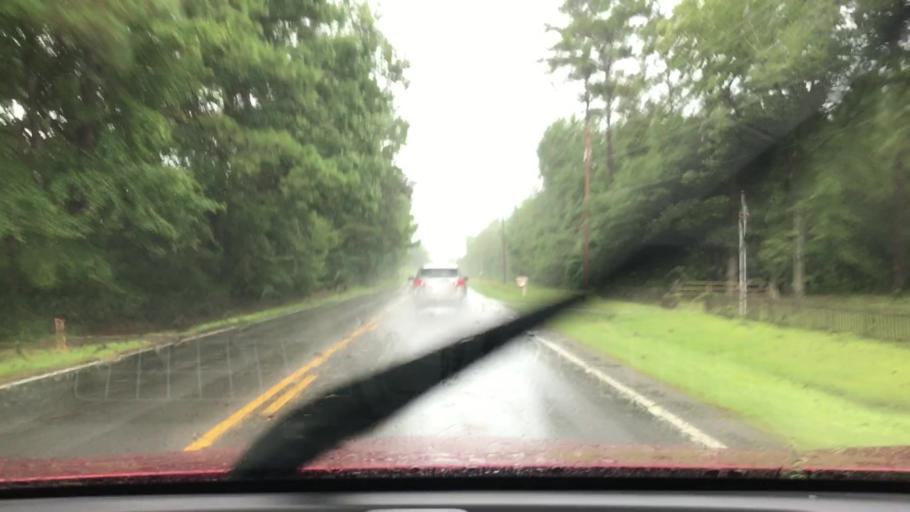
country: US
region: South Carolina
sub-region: Horry County
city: Socastee
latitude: 33.7285
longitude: -79.0841
